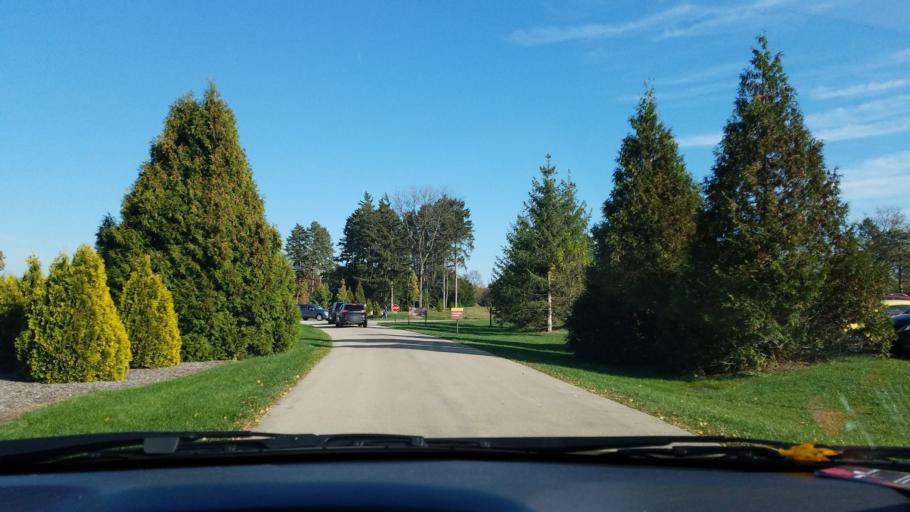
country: US
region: Illinois
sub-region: DuPage County
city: Lisle
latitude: 41.8140
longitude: -88.0765
